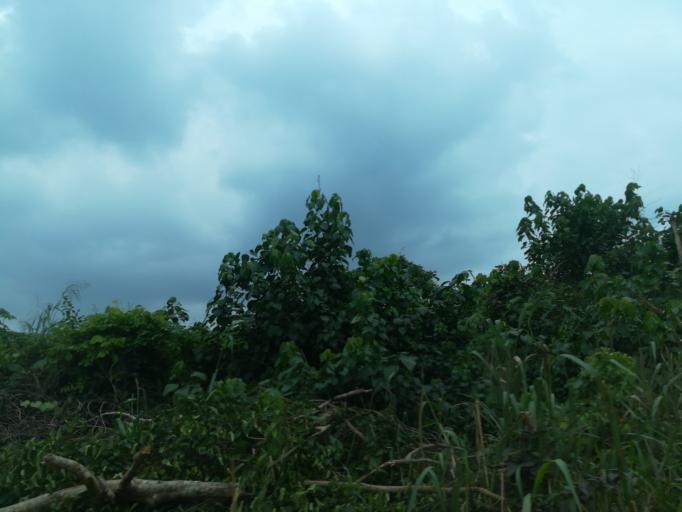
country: NG
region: Lagos
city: Ejirin
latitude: 6.6485
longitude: 3.7406
